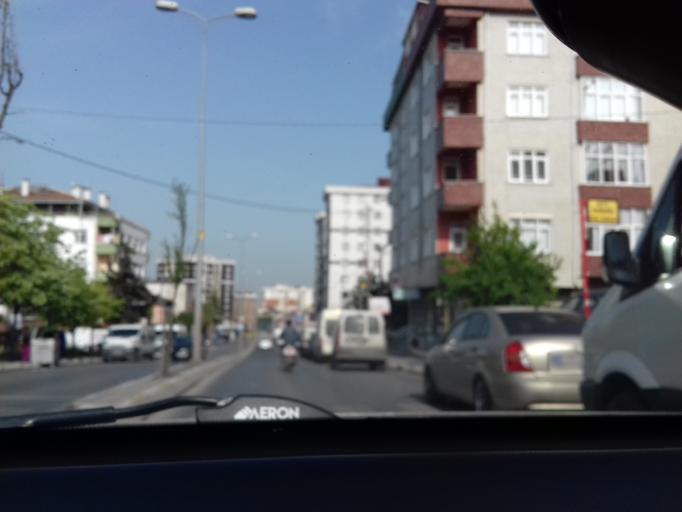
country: TR
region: Istanbul
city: Pendik
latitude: 40.9070
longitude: 29.2506
